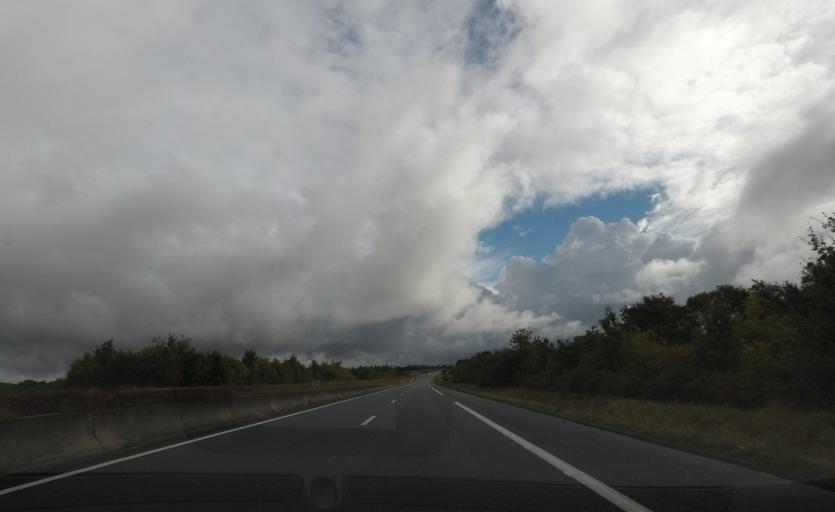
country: FR
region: Pays de la Loire
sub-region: Departement de la Vendee
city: La Roche-sur-Yon
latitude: 46.6495
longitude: -1.3884
